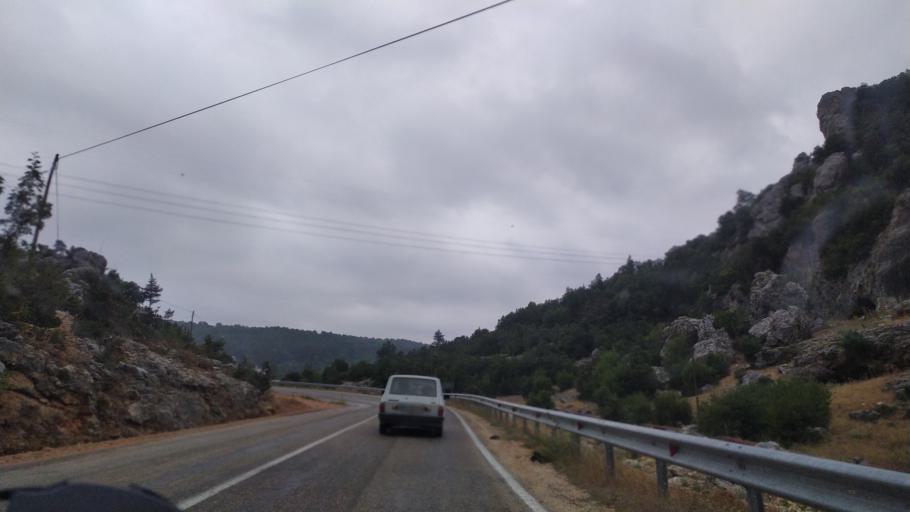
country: TR
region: Mersin
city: Silifke
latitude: 36.5331
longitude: 33.9425
